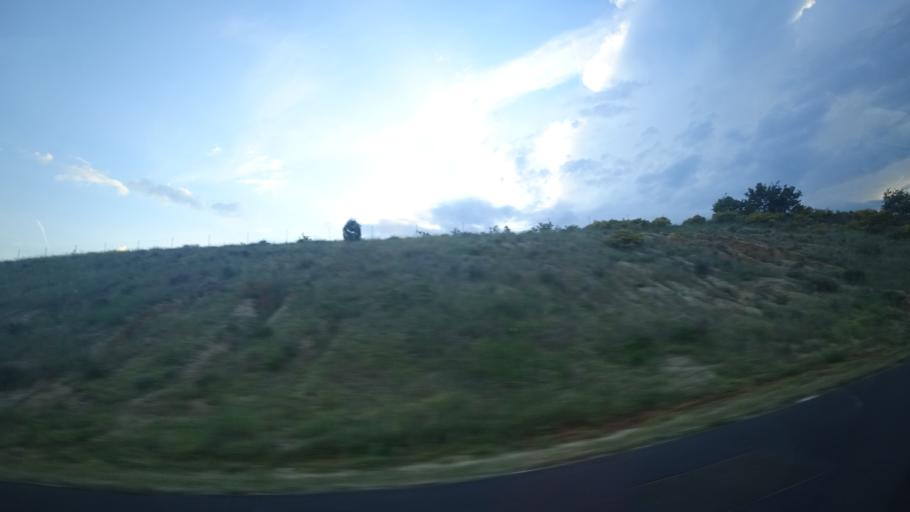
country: FR
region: Languedoc-Roussillon
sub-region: Departement de l'Herault
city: Paulhan
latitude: 43.5324
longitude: 3.4435
